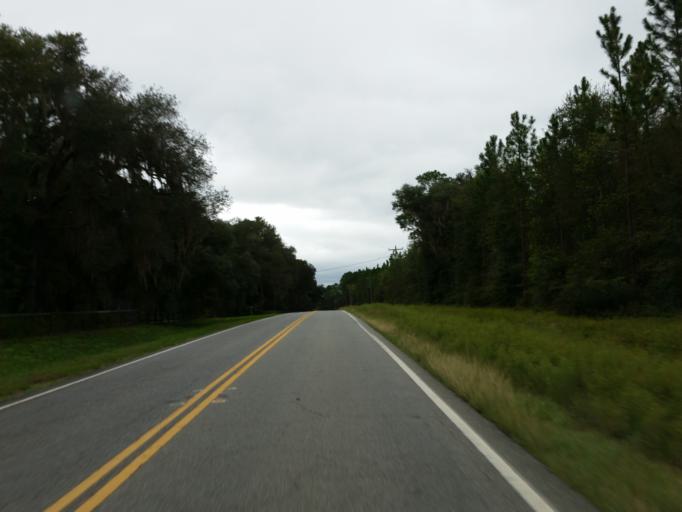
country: US
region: Georgia
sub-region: Echols County
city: Statenville
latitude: 30.8650
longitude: -83.0011
